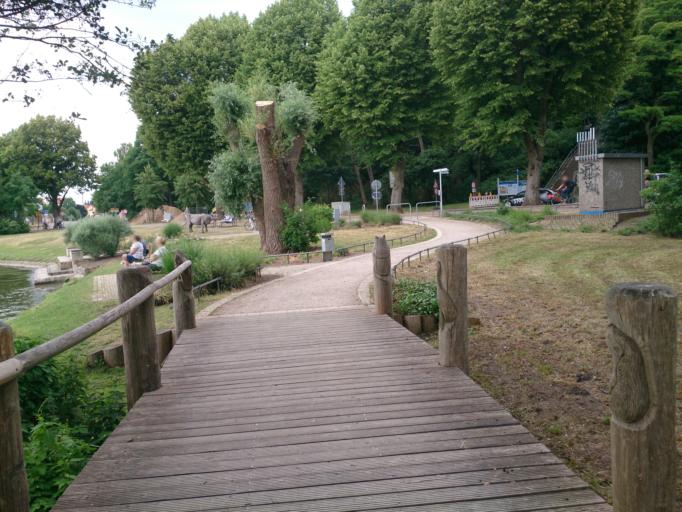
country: DE
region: Mecklenburg-Vorpommern
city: Waren
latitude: 53.5048
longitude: 12.6899
